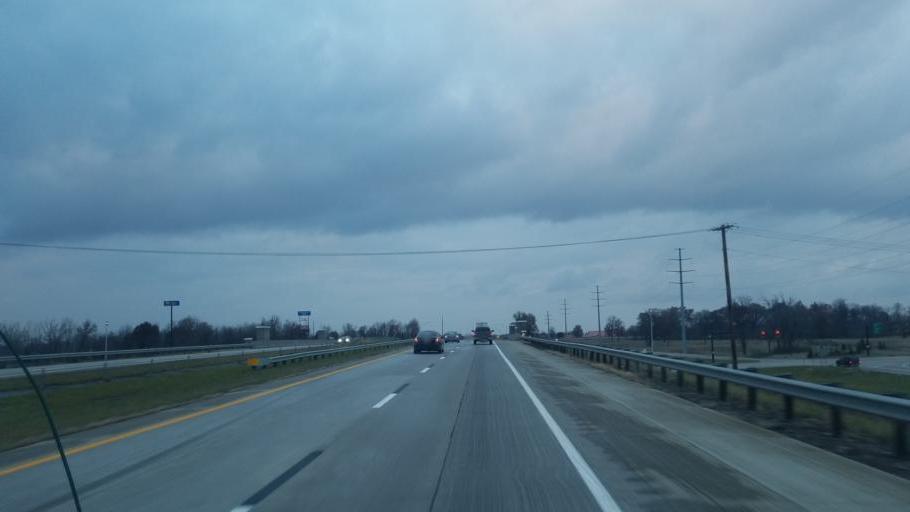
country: US
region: Ohio
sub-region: Allen County
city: Lima
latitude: 40.7547
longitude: -84.0754
